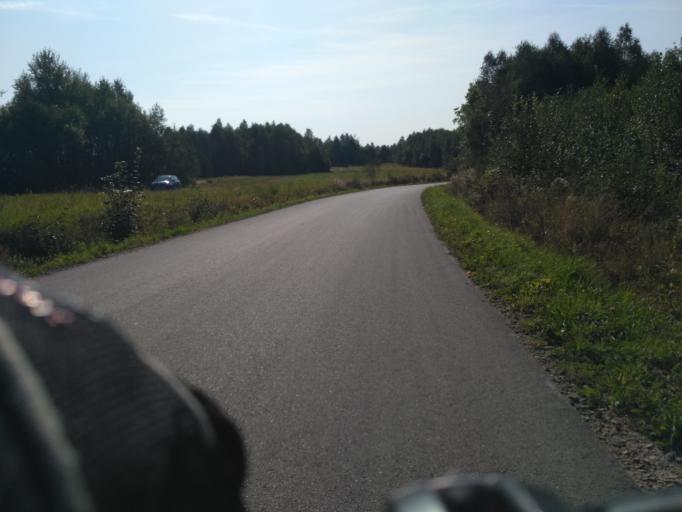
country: PL
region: Subcarpathian Voivodeship
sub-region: Powiat strzyzowski
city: Gwoznica Gorna
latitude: 49.8060
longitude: 22.0240
